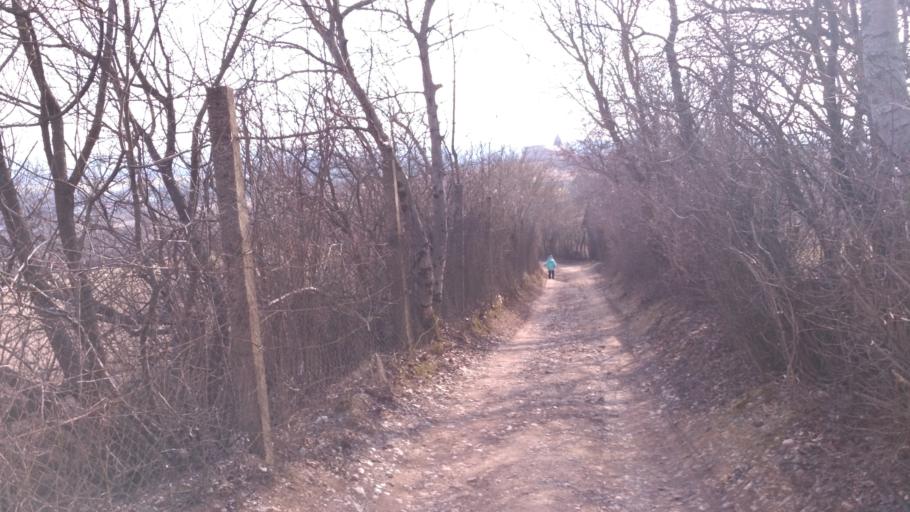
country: SK
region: Kosicky
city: Medzev
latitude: 48.6070
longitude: 20.8756
